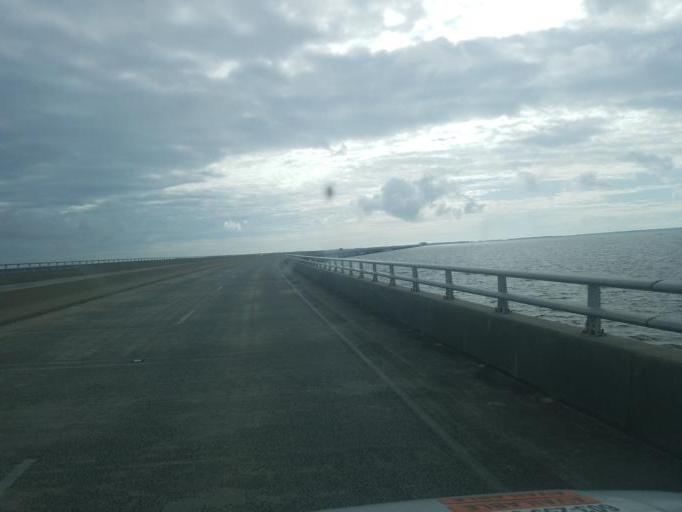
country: US
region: North Carolina
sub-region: Dare County
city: Manteo
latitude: 35.8884
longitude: -75.7540
